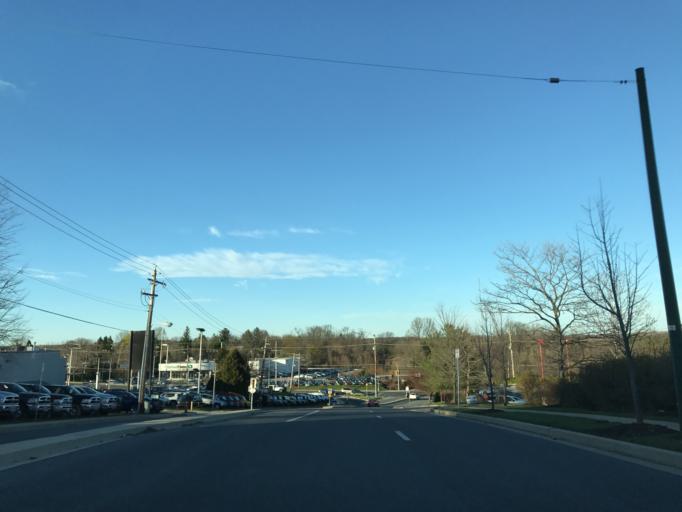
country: US
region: Maryland
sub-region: Baltimore County
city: Owings Mills
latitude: 39.4335
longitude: -76.8002
